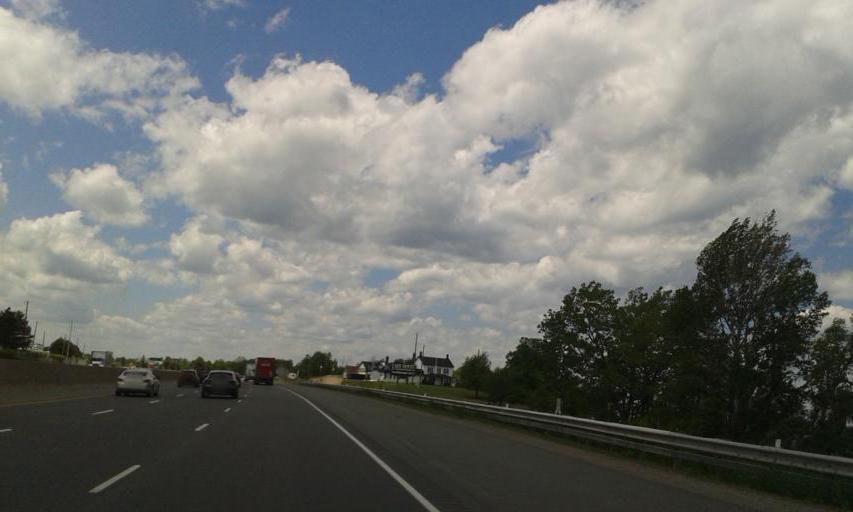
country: CA
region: Ontario
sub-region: Regional Municipality of Niagara
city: St. Catharines
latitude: 43.1856
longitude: -79.3757
